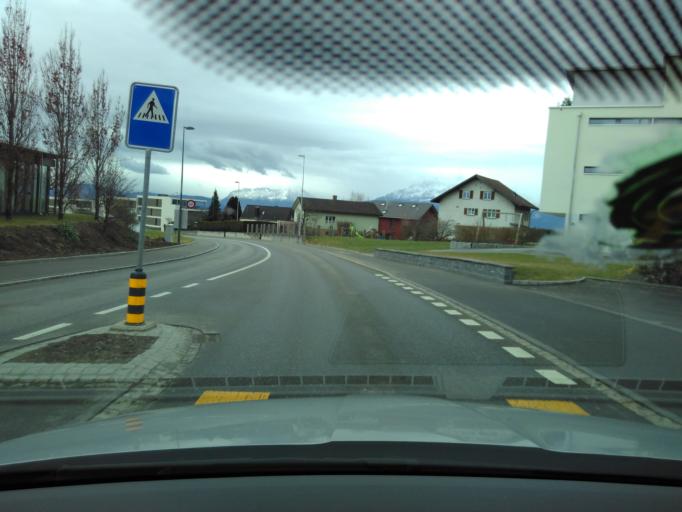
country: CH
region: Lucerne
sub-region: Sursee District
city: Hildisrieden
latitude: 47.1487
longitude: 8.2293
